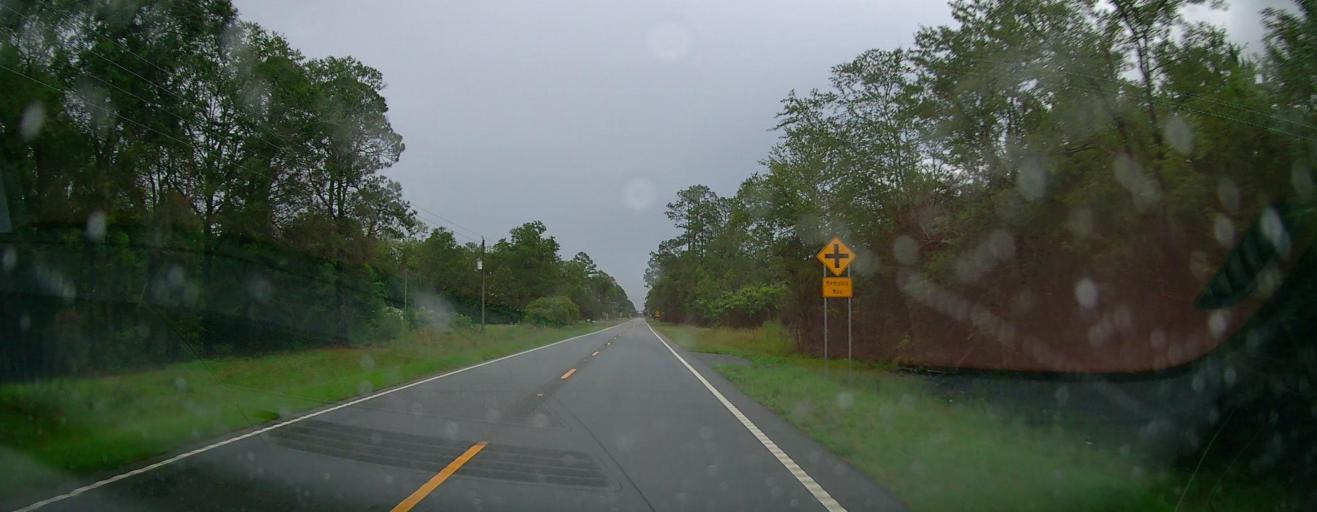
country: US
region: Georgia
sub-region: Brantley County
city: Nahunta
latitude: 31.3374
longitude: -81.9620
